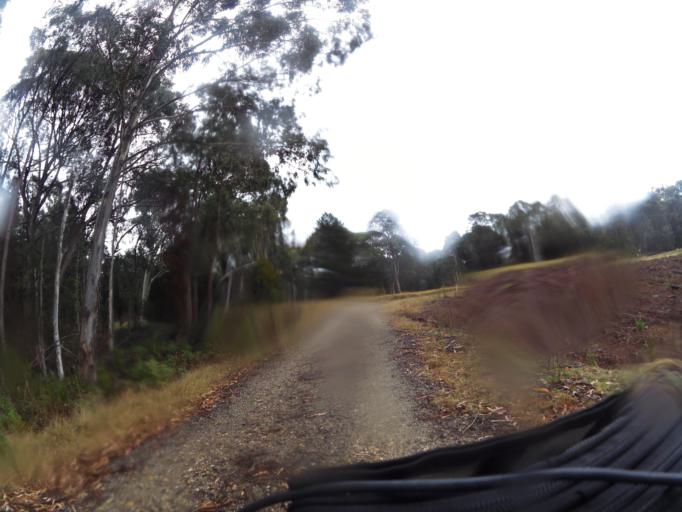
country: AU
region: New South Wales
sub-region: Greater Hume Shire
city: Holbrook
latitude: -36.1880
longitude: 147.5471
